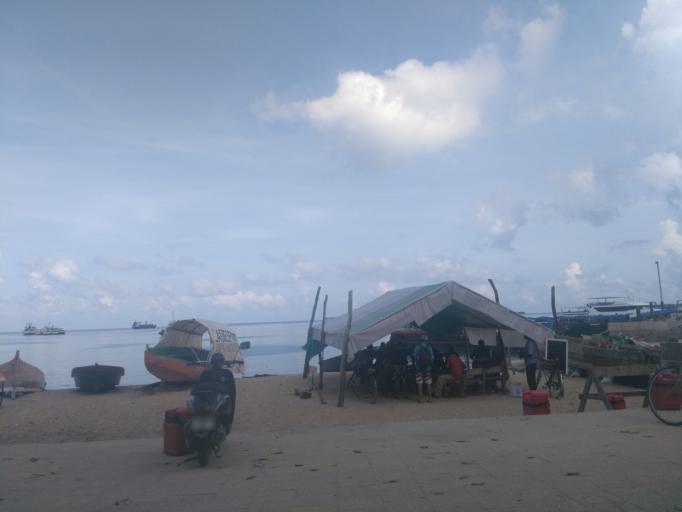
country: TZ
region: Zanzibar Urban/West
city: Zanzibar
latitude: -6.1586
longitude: 39.1919
